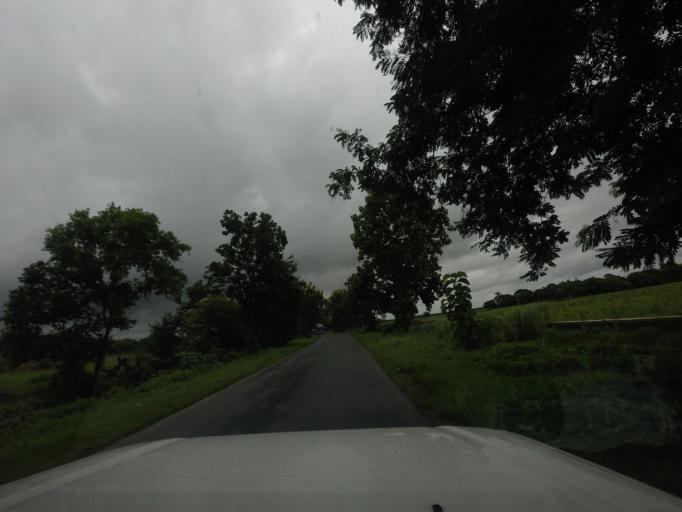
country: MM
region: Ayeyarwady
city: Hinthada
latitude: 17.6186
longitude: 95.4799
